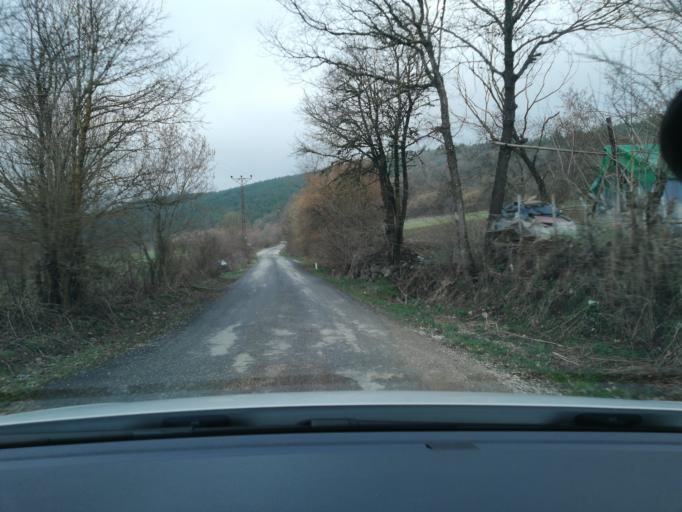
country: TR
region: Bolu
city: Bolu
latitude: 40.6842
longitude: 31.4692
